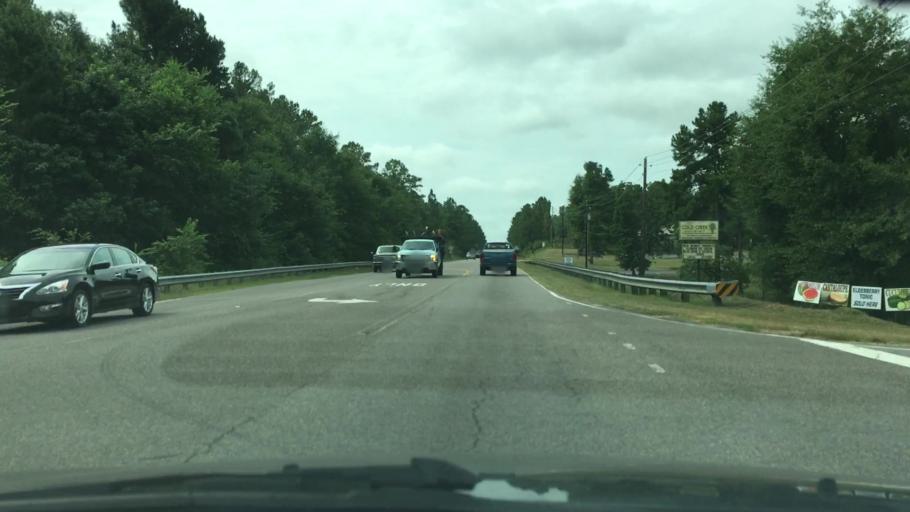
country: US
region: South Carolina
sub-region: Aiken County
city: Warrenville
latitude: 33.5548
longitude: -81.7786
